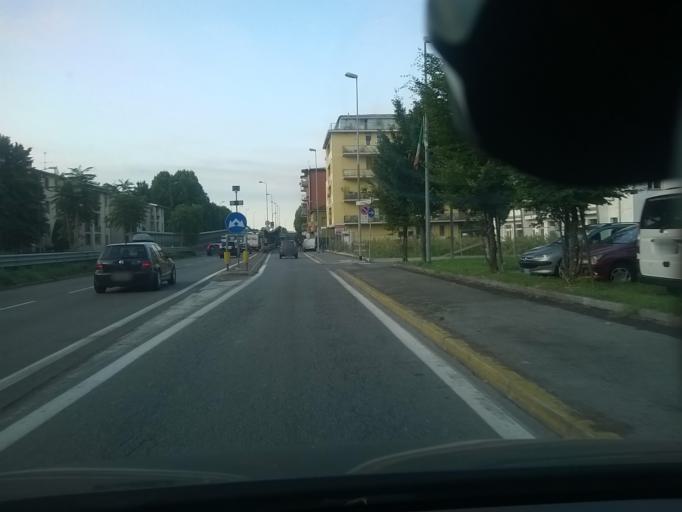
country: IT
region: Lombardy
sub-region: Provincia di Bergamo
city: Gorle
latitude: 45.6959
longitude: 9.6937
